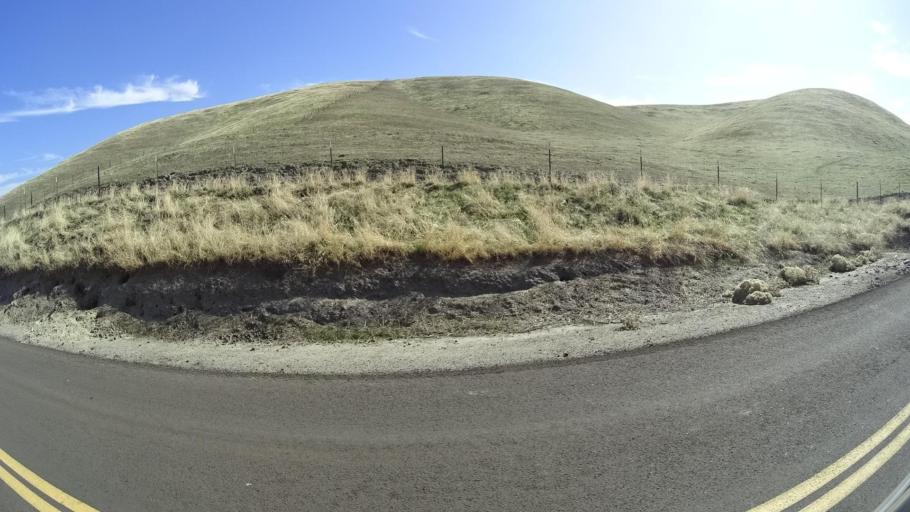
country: US
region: California
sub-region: Tulare County
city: Richgrove
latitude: 35.6705
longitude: -118.9130
